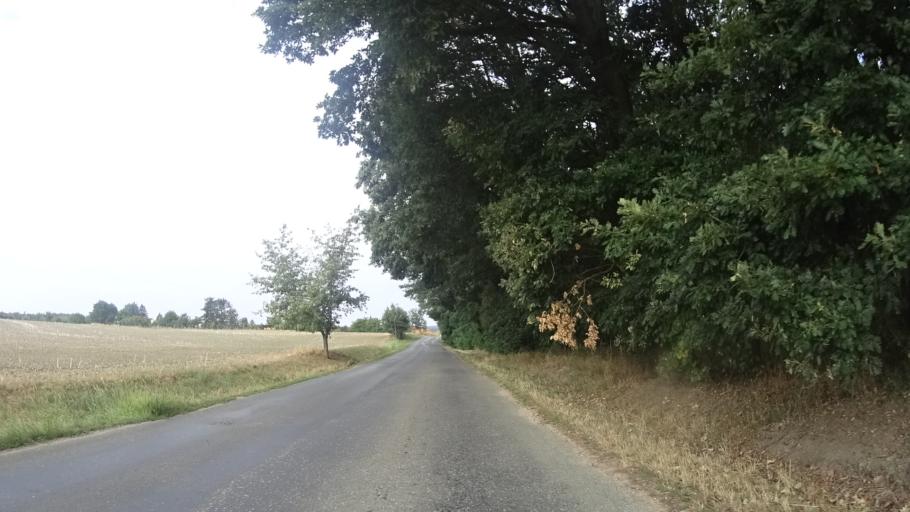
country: CZ
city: Stezery
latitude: 50.2080
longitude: 15.7172
